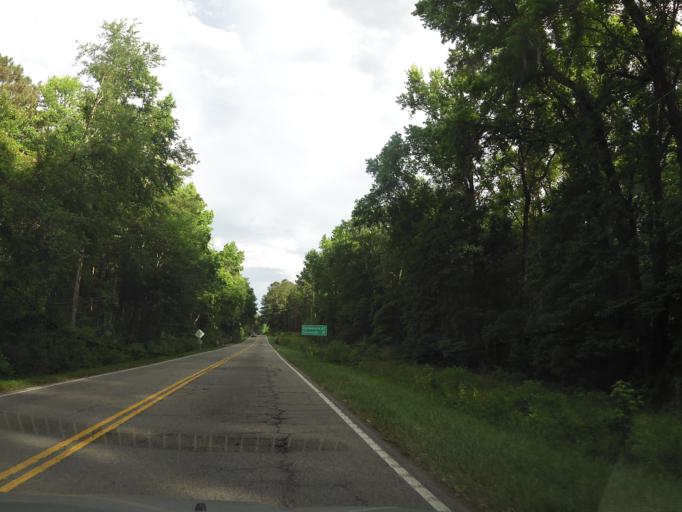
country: US
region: South Carolina
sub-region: Jasper County
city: Ridgeland
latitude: 32.5529
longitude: -81.1684
